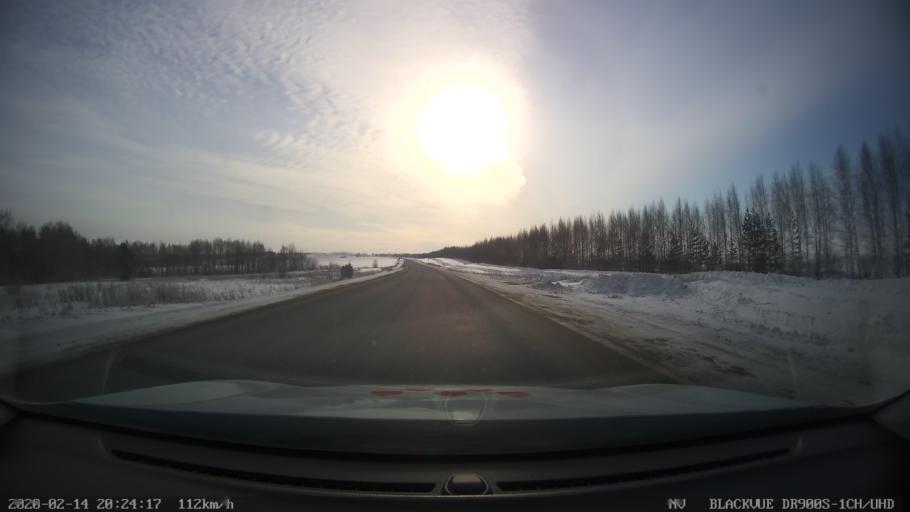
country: RU
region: Tatarstan
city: Verkhniy Uslon
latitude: 55.5149
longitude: 48.9681
